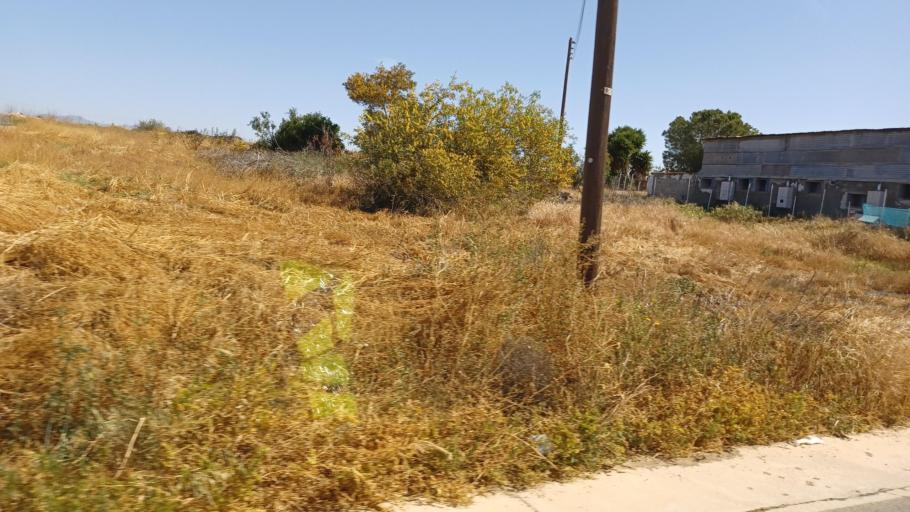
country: CY
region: Lefkosia
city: Kokkinotrimithia
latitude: 35.1581
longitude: 33.1756
